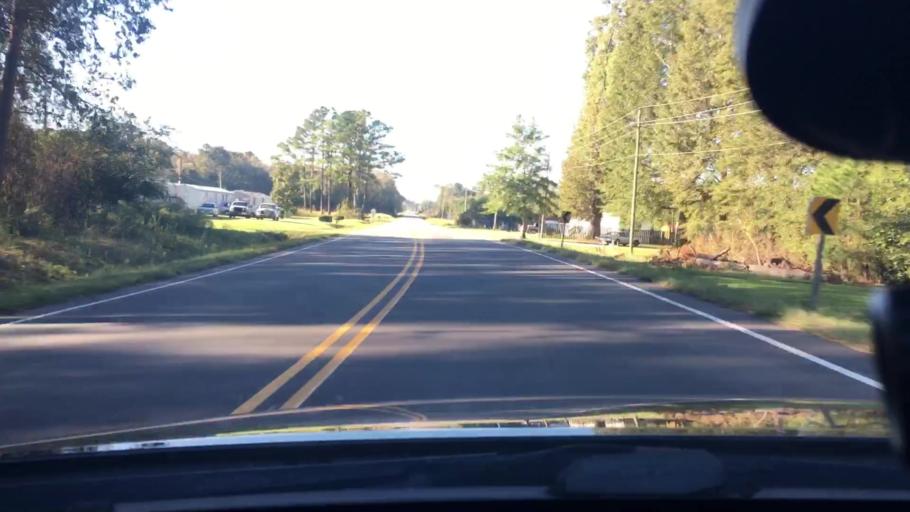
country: US
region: North Carolina
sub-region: Pitt County
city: Windsor
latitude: 35.4530
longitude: -77.2644
